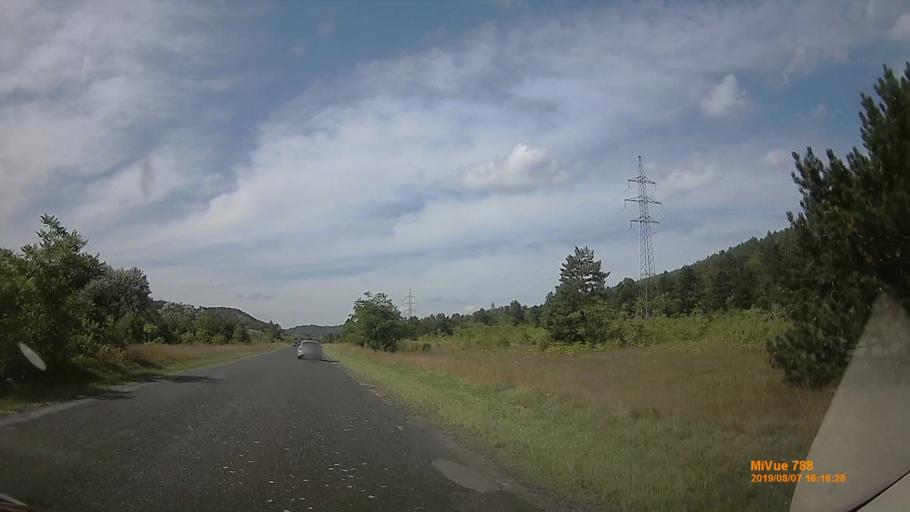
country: HU
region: Zala
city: Gyenesdias
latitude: 46.8133
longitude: 17.2703
